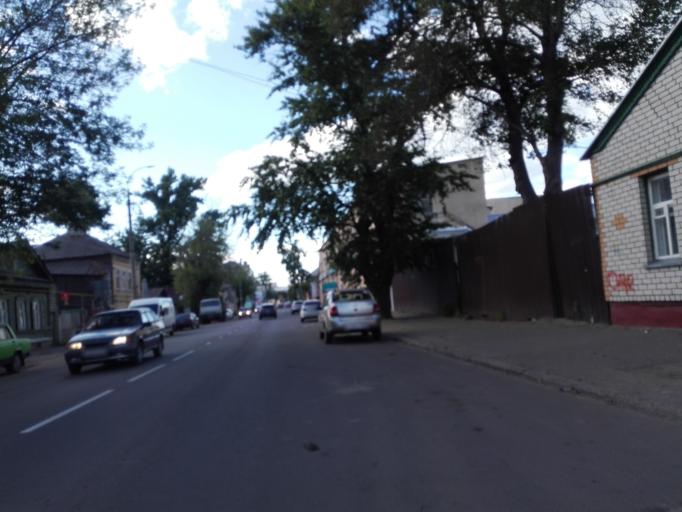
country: RU
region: Orjol
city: Orel
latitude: 52.9595
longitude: 36.0715
